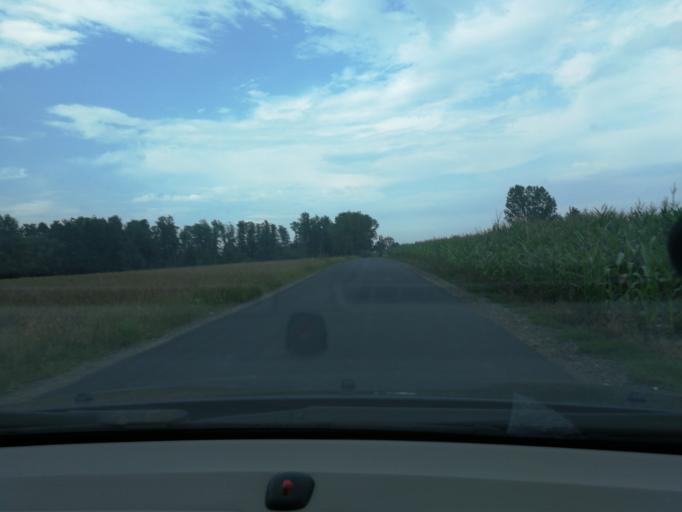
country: PL
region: Masovian Voivodeship
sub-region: Powiat warszawski zachodni
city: Bieniewice
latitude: 52.1156
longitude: 20.5570
